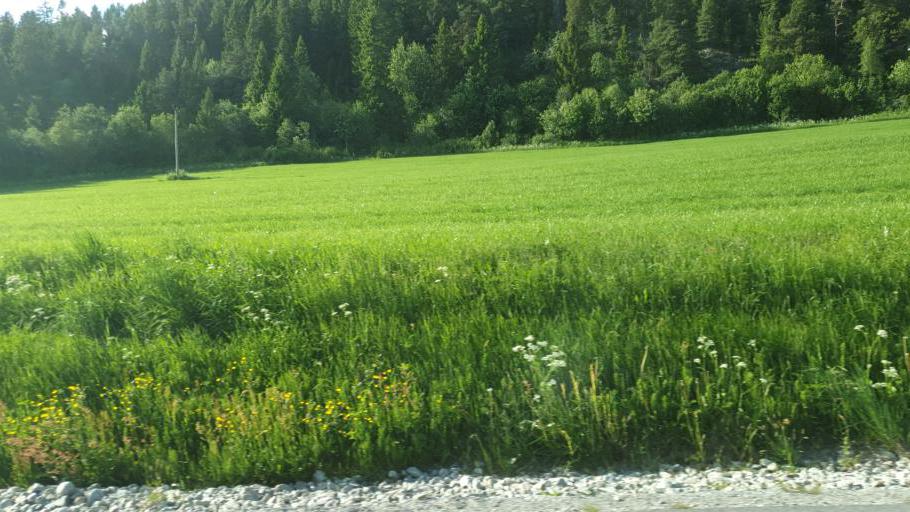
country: NO
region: Sor-Trondelag
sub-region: Rissa
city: Rissa
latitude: 63.4978
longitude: 10.1095
